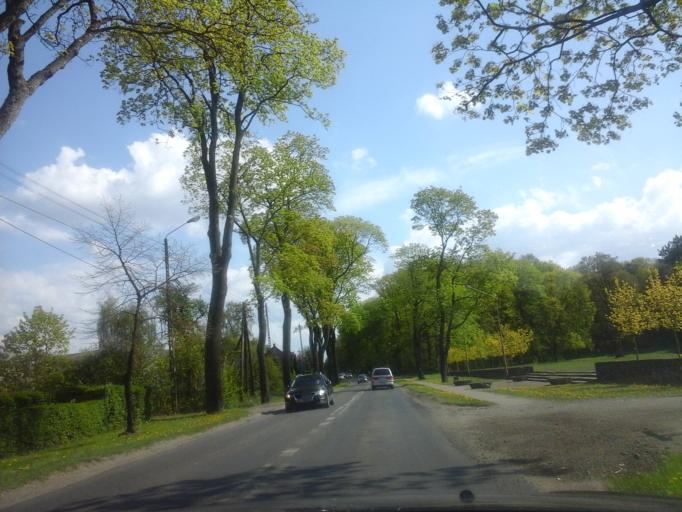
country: PL
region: West Pomeranian Voivodeship
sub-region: Powiat choszczenski
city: Choszczno
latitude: 53.1625
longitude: 15.4297
